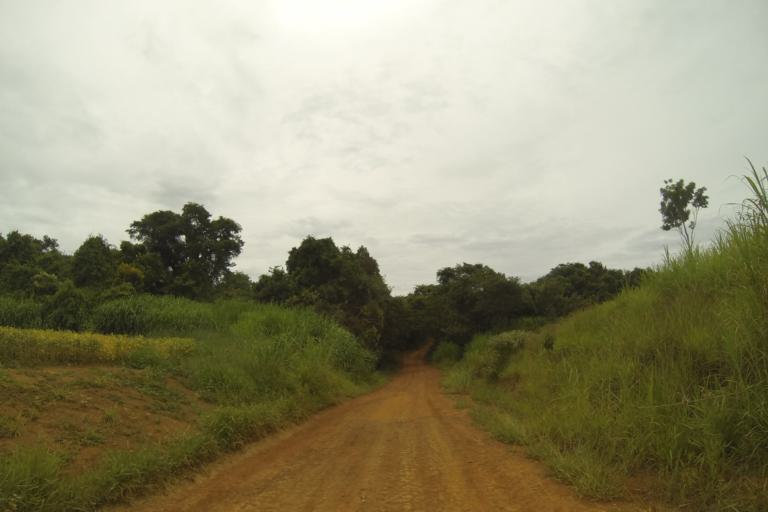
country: BR
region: Minas Gerais
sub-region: Ibia
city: Ibia
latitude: -19.7458
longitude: -46.6290
